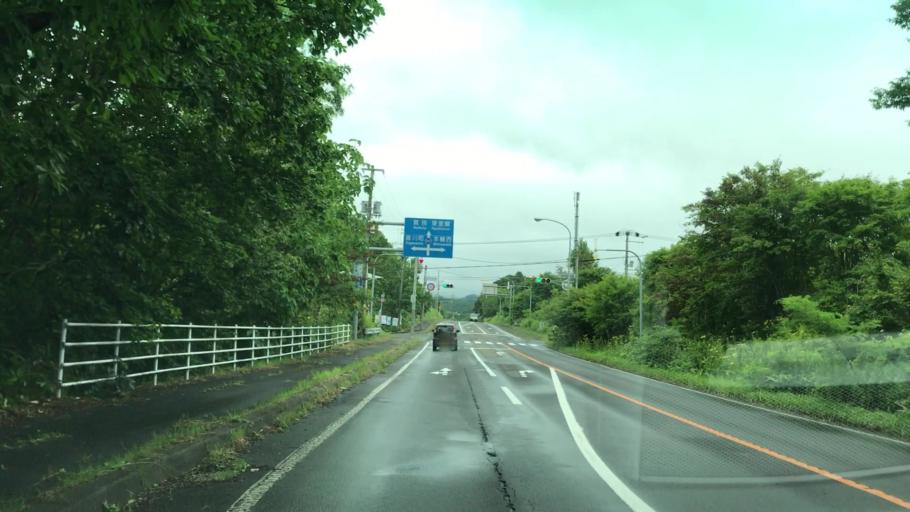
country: JP
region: Hokkaido
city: Muroran
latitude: 42.3865
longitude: 140.9842
